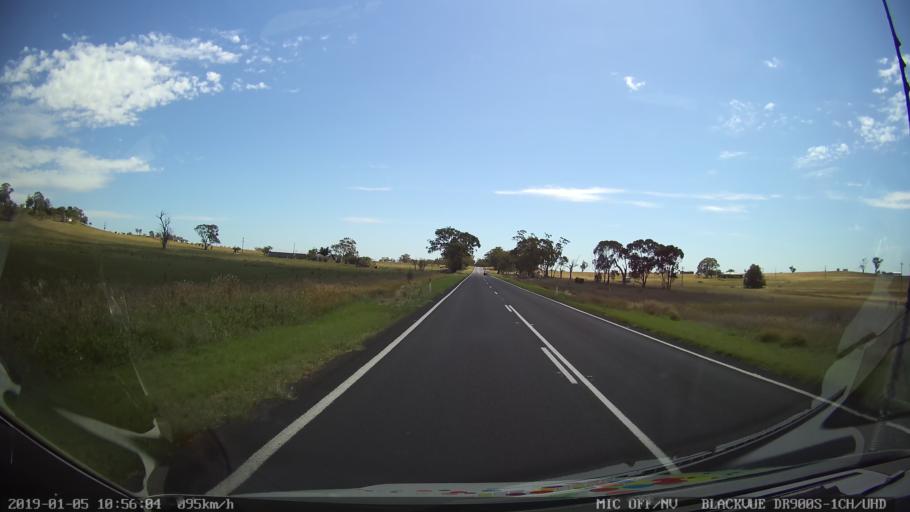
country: AU
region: New South Wales
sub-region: Warrumbungle Shire
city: Coonabarabran
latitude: -31.4444
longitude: 149.1532
